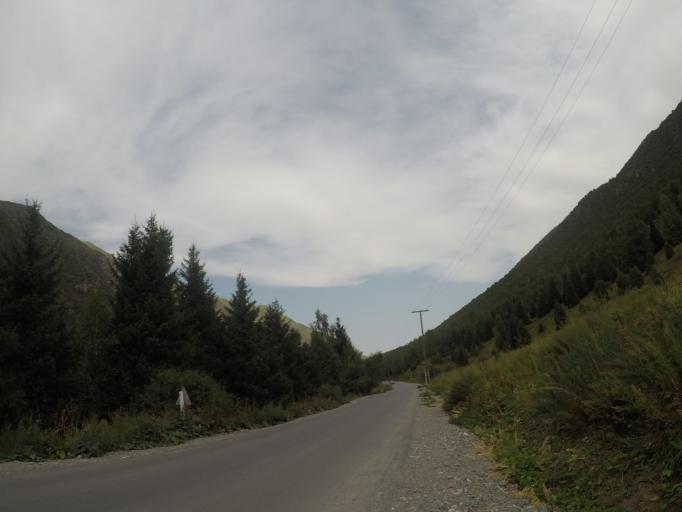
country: KG
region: Chuy
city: Bishkek
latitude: 42.5921
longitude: 74.4834
